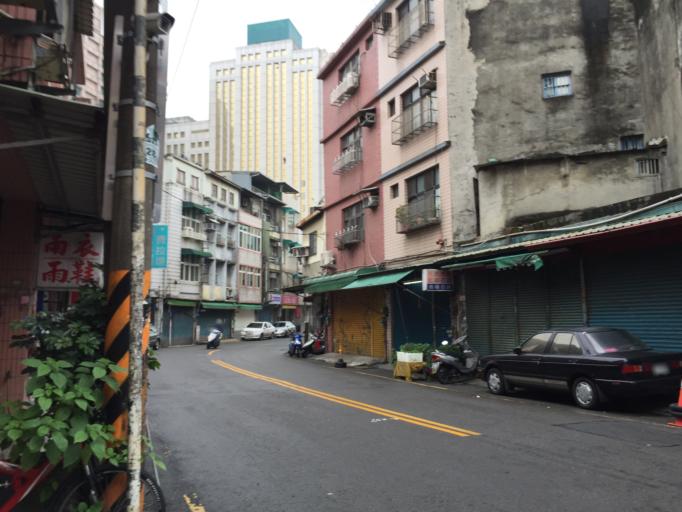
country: TW
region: Taiwan
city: Taoyuan City
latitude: 24.9559
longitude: 121.2279
